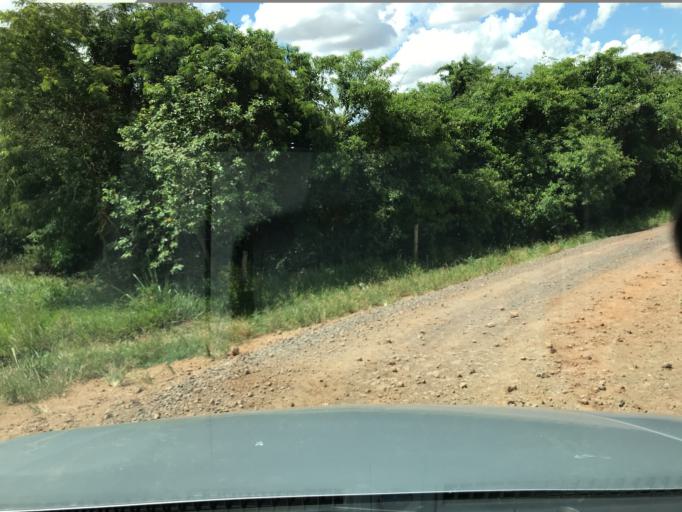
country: BR
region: Parana
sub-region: Palotina
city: Palotina
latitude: -24.1786
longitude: -53.7775
